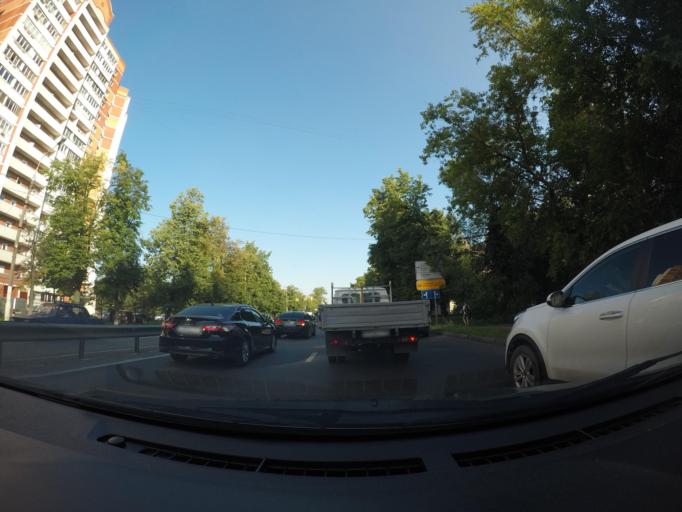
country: RU
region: Moscow
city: Zhulebino
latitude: 55.6930
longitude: 37.8656
